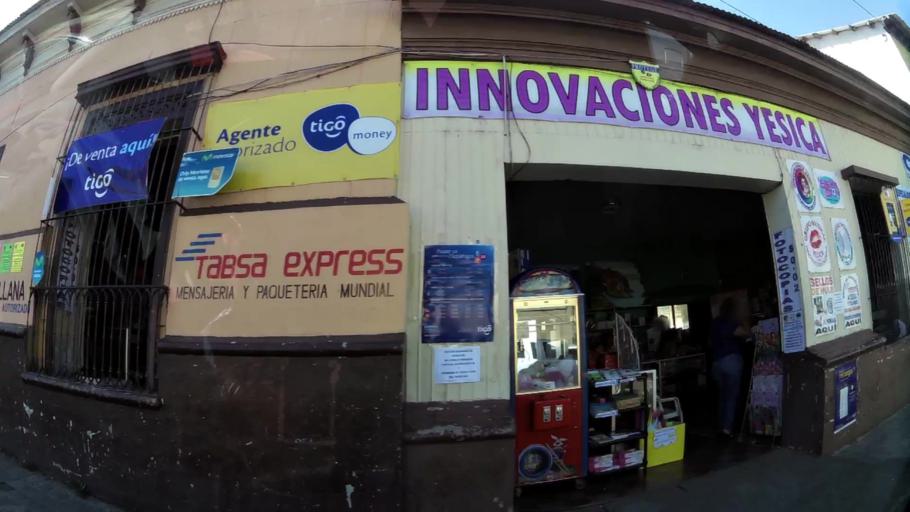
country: SV
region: Ahuachapan
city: Ahuachapan
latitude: 13.9198
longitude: -89.8468
